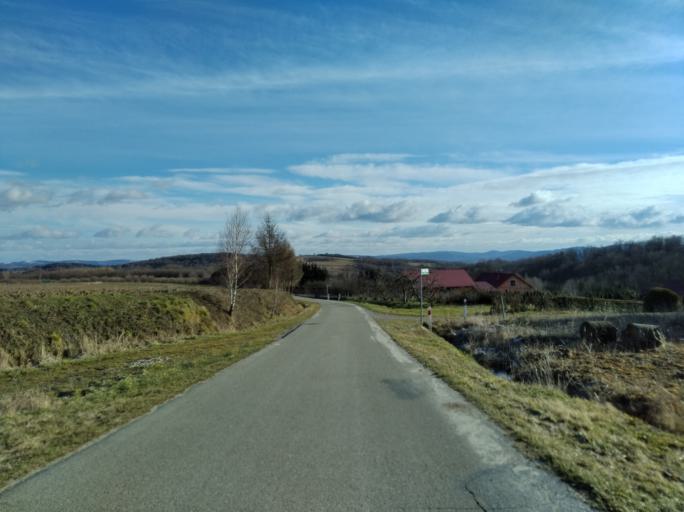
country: PL
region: Subcarpathian Voivodeship
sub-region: Powiat strzyzowski
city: Wisniowa
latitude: 49.9032
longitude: 21.6560
